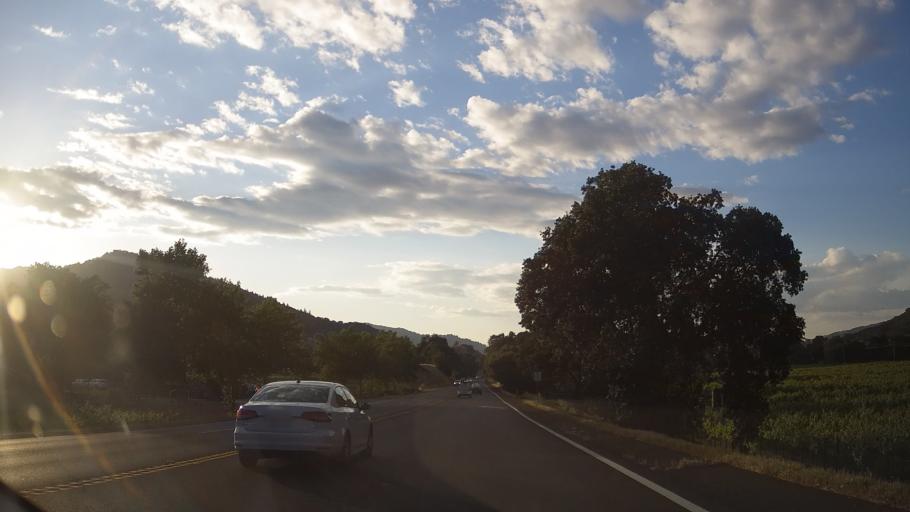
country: US
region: California
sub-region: Mendocino County
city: Talmage
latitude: 39.0132
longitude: -123.1267
